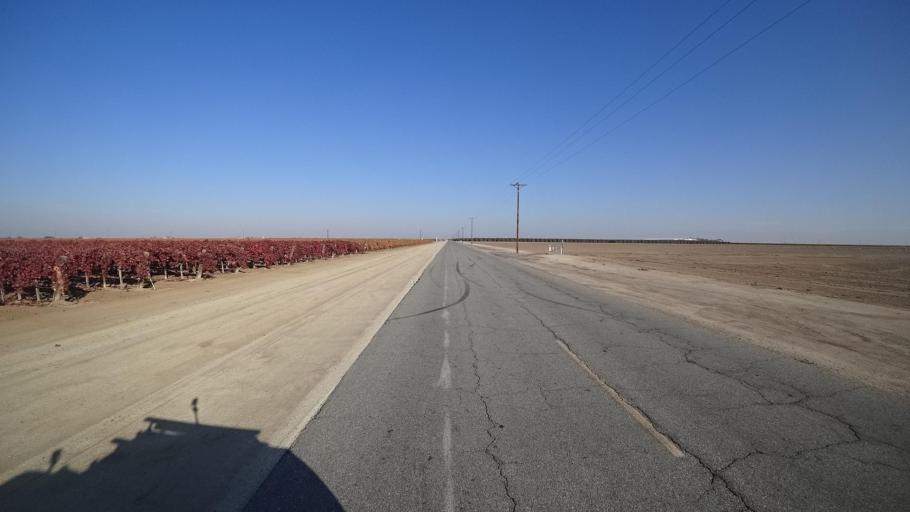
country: US
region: California
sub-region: Tulare County
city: Richgrove
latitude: 35.7794
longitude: -119.1701
